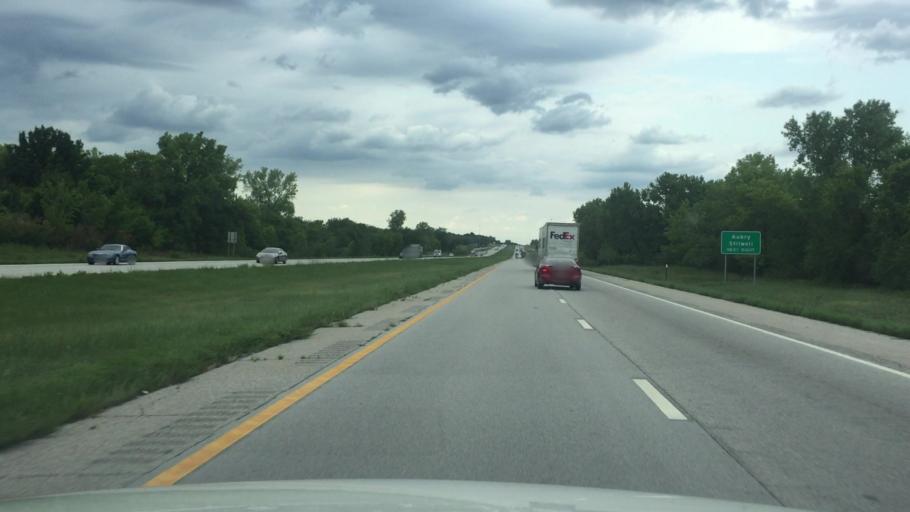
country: US
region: Kansas
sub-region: Miami County
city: Louisburg
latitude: 38.7579
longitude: -94.6775
